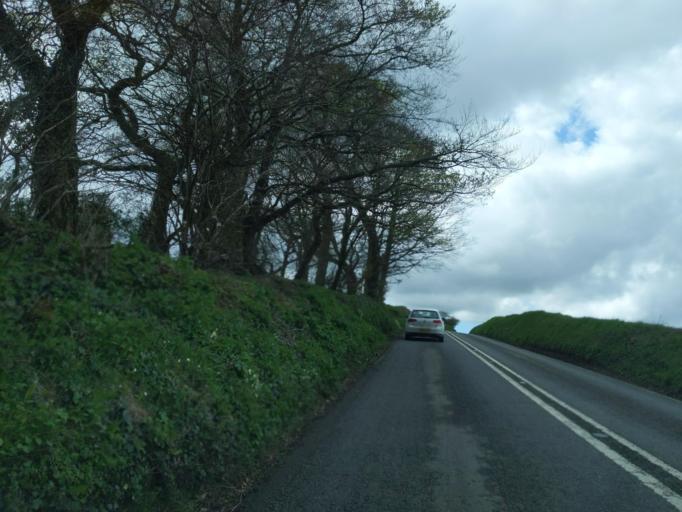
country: GB
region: England
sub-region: Cornwall
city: Callington
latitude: 50.4858
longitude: -4.3536
